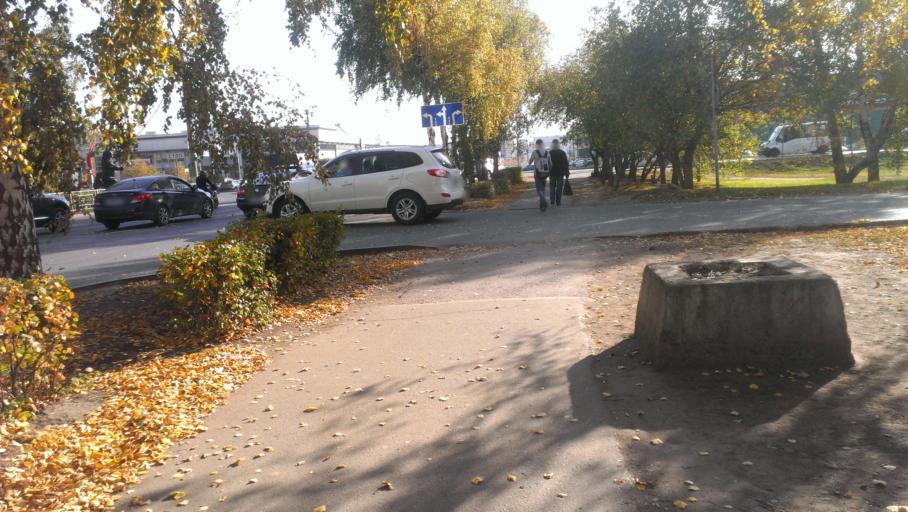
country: RU
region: Altai Krai
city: Novosilikatnyy
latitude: 53.3439
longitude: 83.6839
